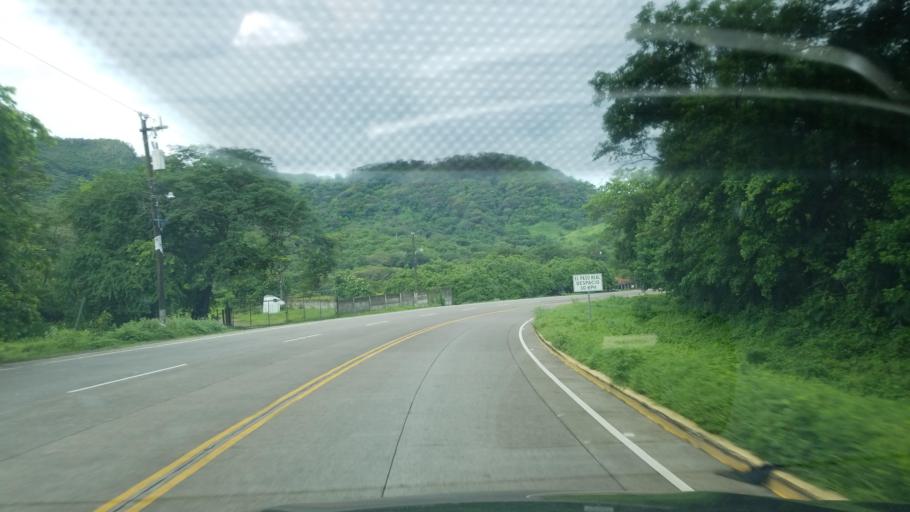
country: HN
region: Francisco Morazan
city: El Porvenir
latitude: 13.6896
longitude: -87.3301
